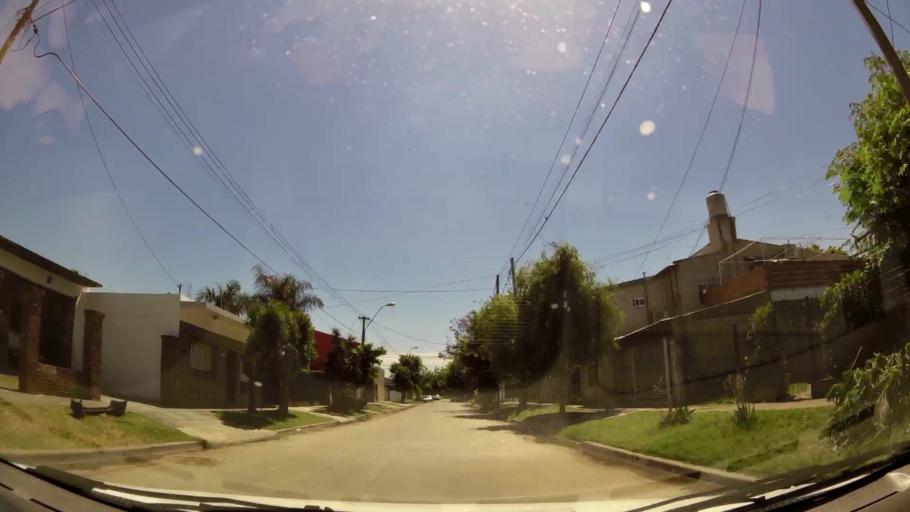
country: AR
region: Buenos Aires
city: Ituzaingo
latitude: -34.6754
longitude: -58.6715
